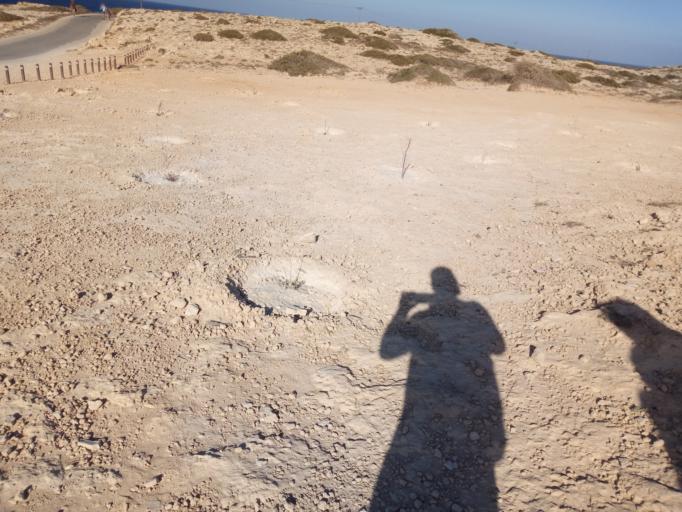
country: CY
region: Ammochostos
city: Protaras
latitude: 34.9654
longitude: 34.0770
